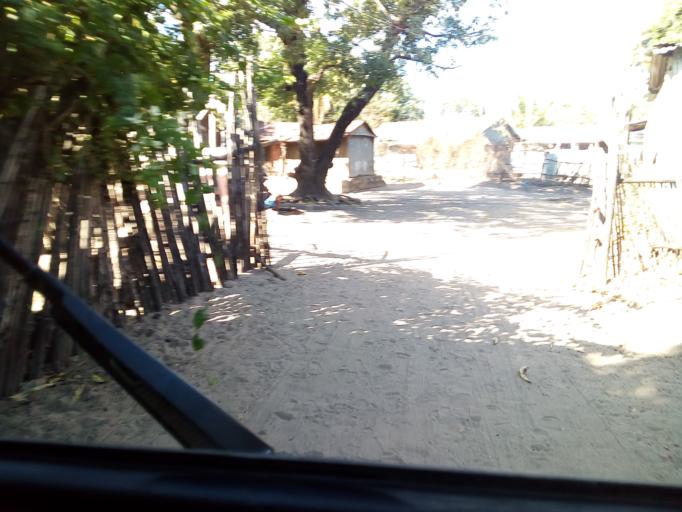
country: MG
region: Boeny
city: Mahajanga
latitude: -15.7110
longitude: 46.3378
